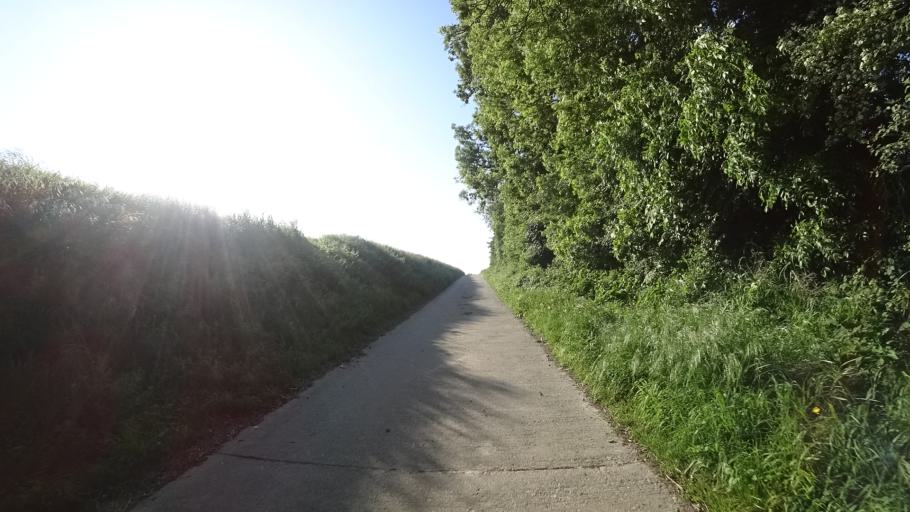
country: BE
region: Wallonia
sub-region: Province du Brabant Wallon
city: Walhain-Saint-Paul
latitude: 50.6252
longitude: 4.7009
